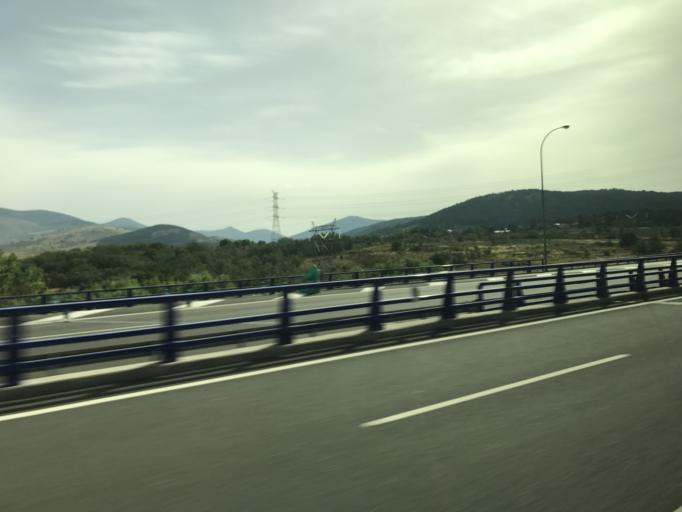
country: ES
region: Castille and Leon
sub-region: Provincia de Segovia
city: Otero de Herreros
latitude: 40.7334
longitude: -4.2002
